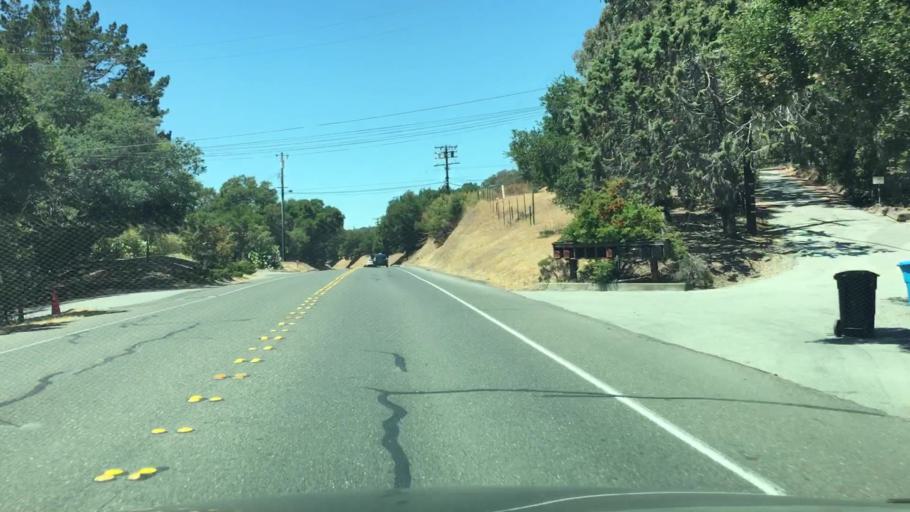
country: US
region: California
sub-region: San Mateo County
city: Emerald Lake Hills
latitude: 37.4750
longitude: -122.2651
